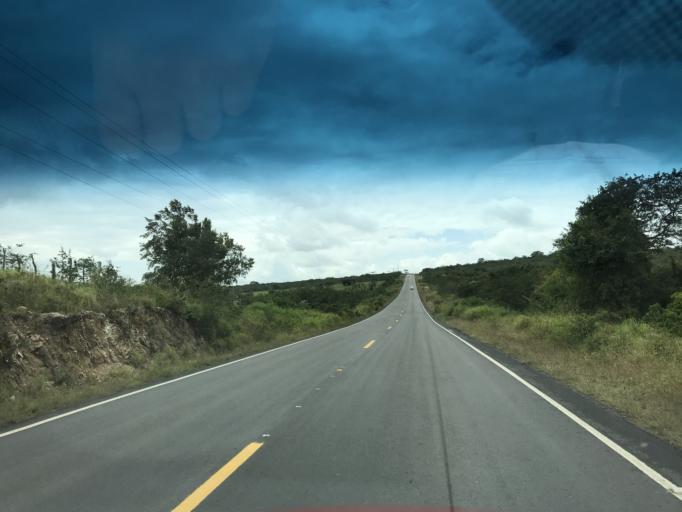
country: BR
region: Bahia
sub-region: Conceicao Do Almeida
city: Conceicao do Almeida
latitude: -12.6704
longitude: -39.2893
